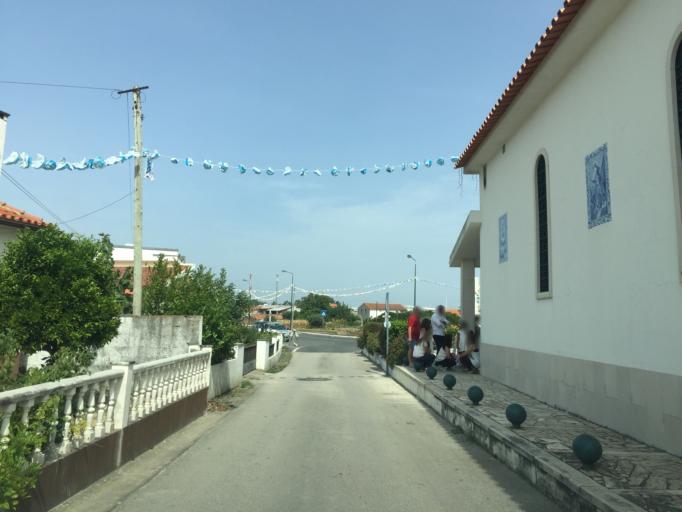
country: PT
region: Leiria
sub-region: Batalha
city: Batalha
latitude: 39.6642
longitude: -8.8331
